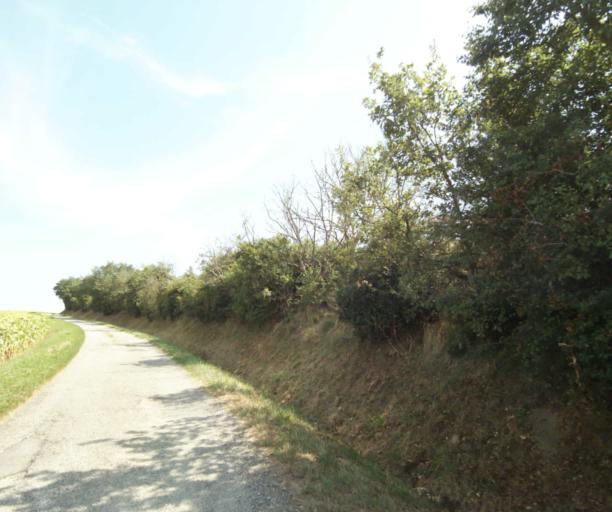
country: FR
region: Midi-Pyrenees
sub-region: Departement de l'Ariege
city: Lezat-sur-Leze
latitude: 43.2515
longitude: 1.4058
